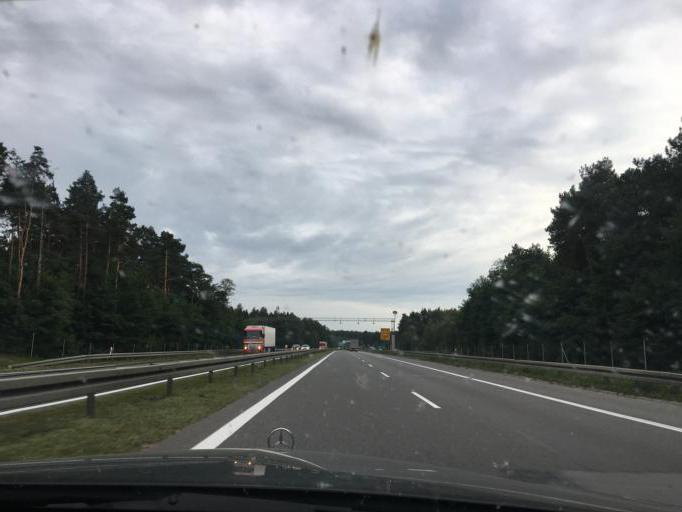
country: PL
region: Masovian Voivodeship
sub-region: Powiat ostrowski
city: Ostrow Mazowiecka
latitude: 52.7950
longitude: 21.8678
